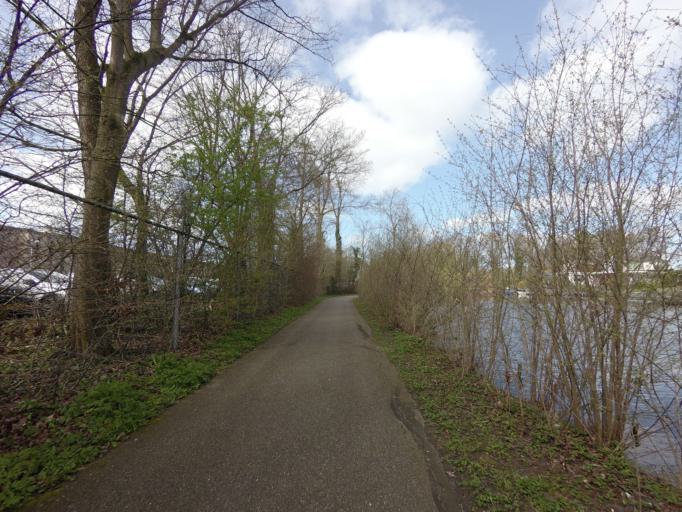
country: NL
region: Utrecht
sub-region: Stichtse Vecht
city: Maarssen
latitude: 52.1459
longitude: 5.0846
